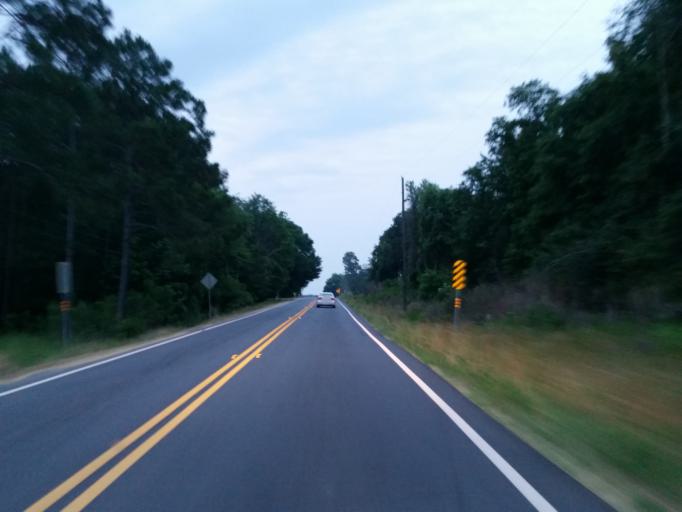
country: US
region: Georgia
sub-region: Turner County
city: Ashburn
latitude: 31.7545
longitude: -83.6795
